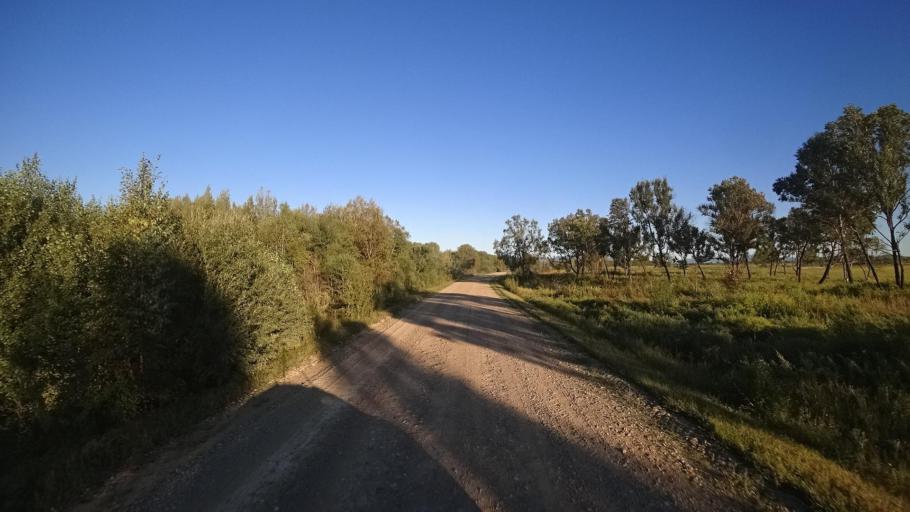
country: RU
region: Primorskiy
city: Kirovskiy
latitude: 44.8264
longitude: 133.5950
